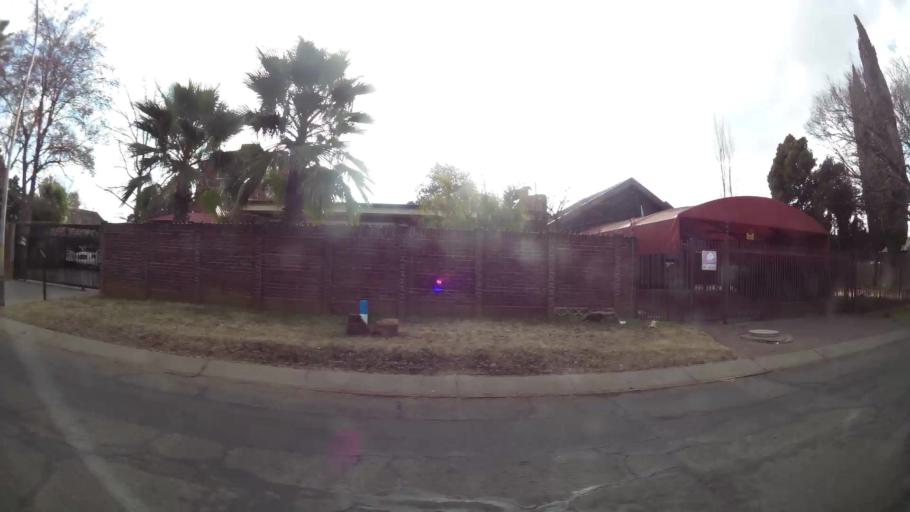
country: ZA
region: Orange Free State
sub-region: Mangaung Metropolitan Municipality
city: Bloemfontein
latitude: -29.1015
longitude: 26.2013
